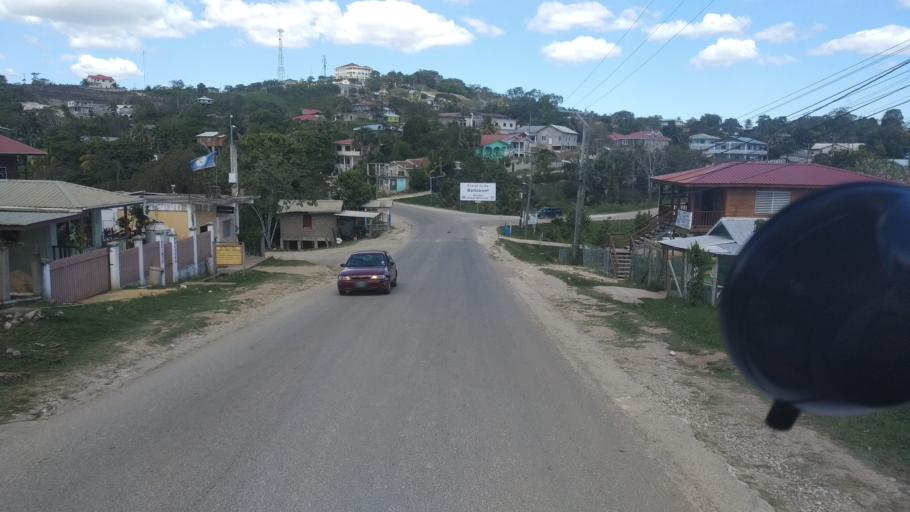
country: BZ
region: Cayo
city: Benque Viejo del Carmen
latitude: 17.0748
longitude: -89.1349
